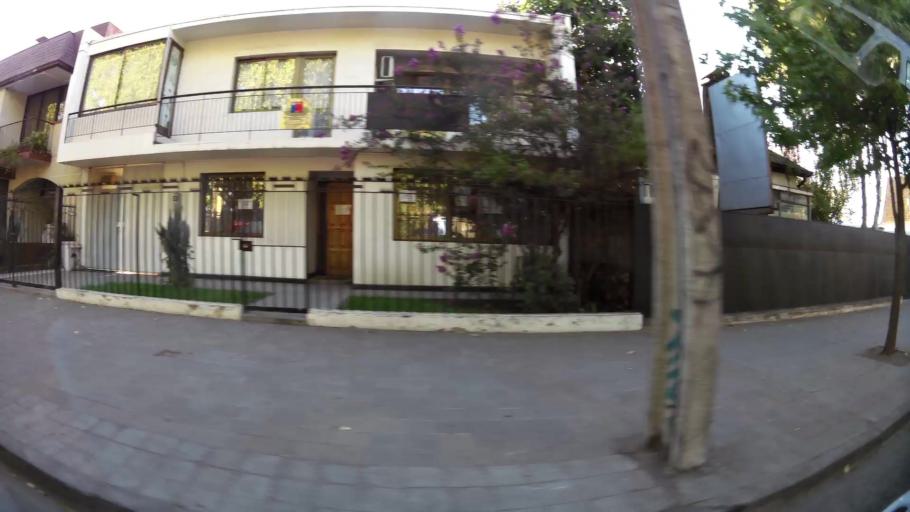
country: CL
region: Maule
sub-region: Provincia de Curico
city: Curico
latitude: -34.9840
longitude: -71.2346
